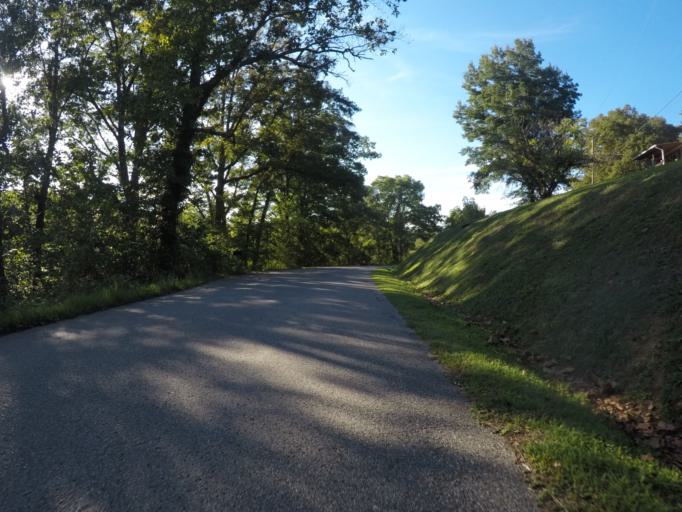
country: US
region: West Virginia
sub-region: Cabell County
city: Huntington
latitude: 38.5147
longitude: -82.4996
